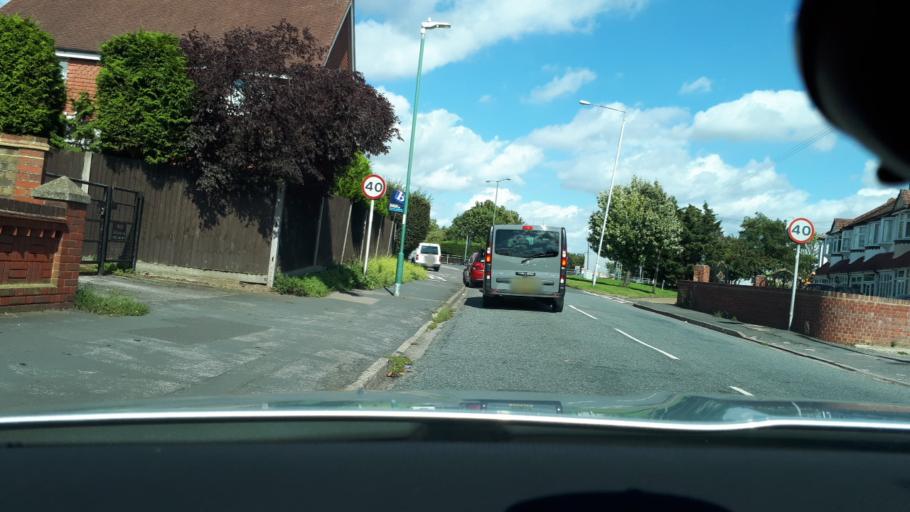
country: GB
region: England
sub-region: Kent
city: Dartford
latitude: 51.4385
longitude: 0.1996
